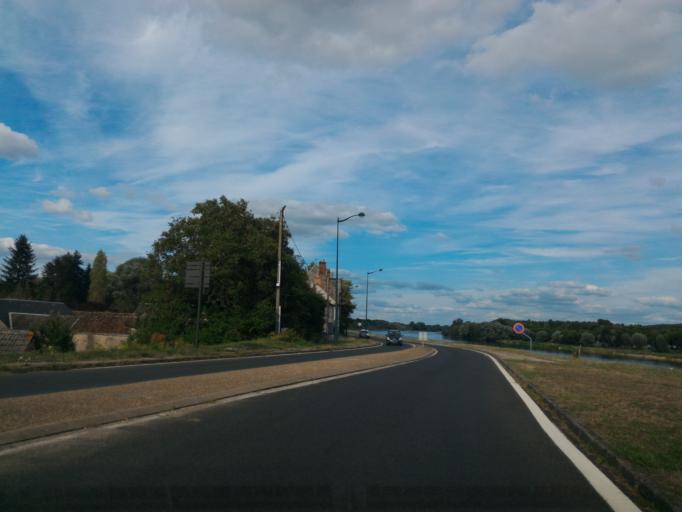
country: FR
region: Centre
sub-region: Departement du Loir-et-Cher
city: Chaumont-sur-Loire
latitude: 47.4869
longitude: 1.1897
